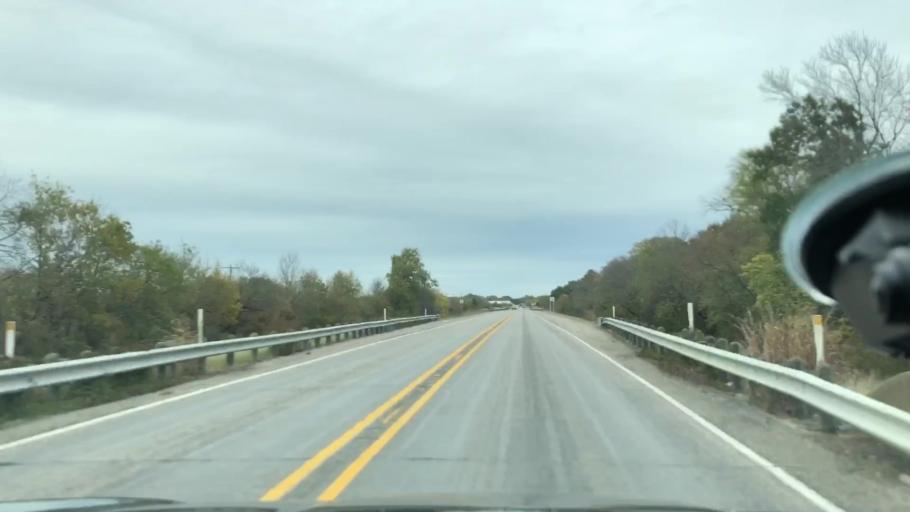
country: US
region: Texas
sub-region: Hunt County
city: Quinlan
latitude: 32.9369
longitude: -96.1144
